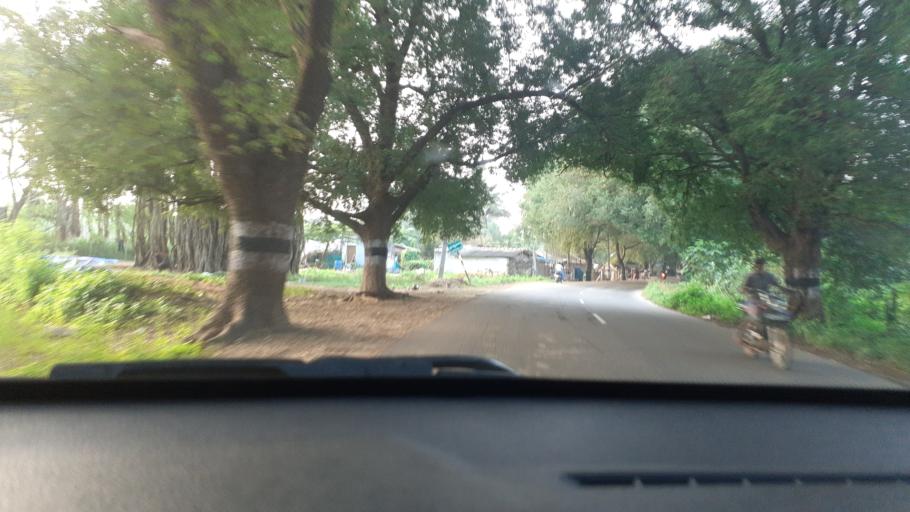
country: IN
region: Tamil Nadu
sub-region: Dindigul
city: Ayakudi
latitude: 10.4092
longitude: 77.5397
